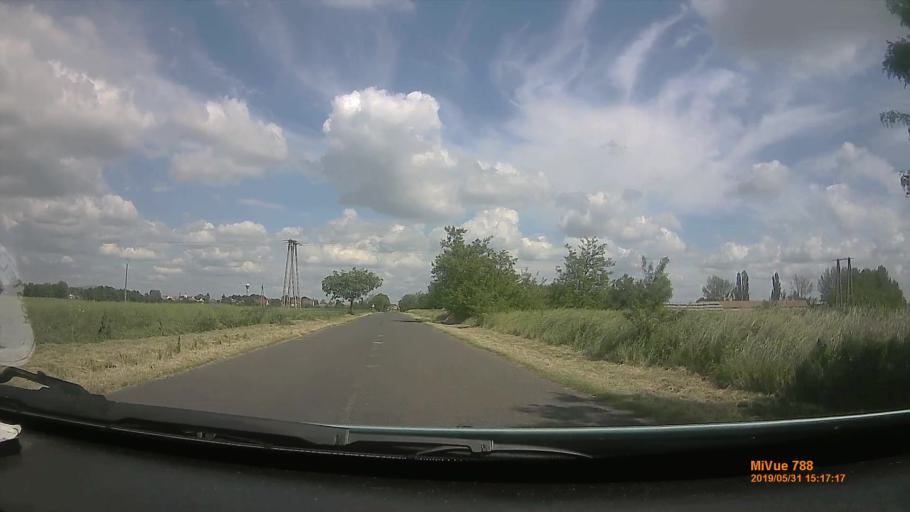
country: HU
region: Borsod-Abauj-Zemplen
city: Taktaharkany
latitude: 48.0840
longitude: 21.1169
